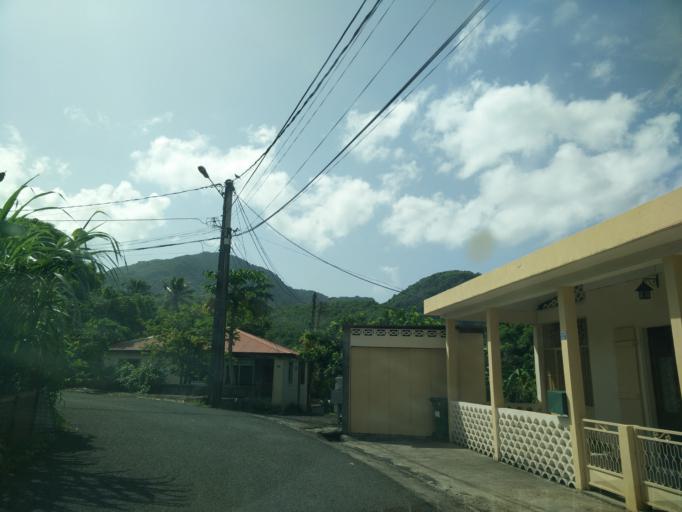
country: GP
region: Guadeloupe
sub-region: Guadeloupe
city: Gourbeyre
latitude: 15.9930
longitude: -61.7069
